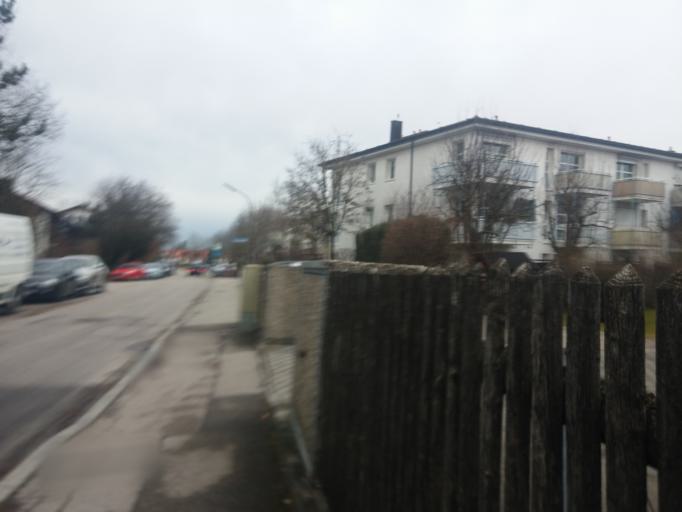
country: DE
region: Bavaria
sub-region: Upper Bavaria
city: Taufkirchen
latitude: 48.0507
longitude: 11.6257
